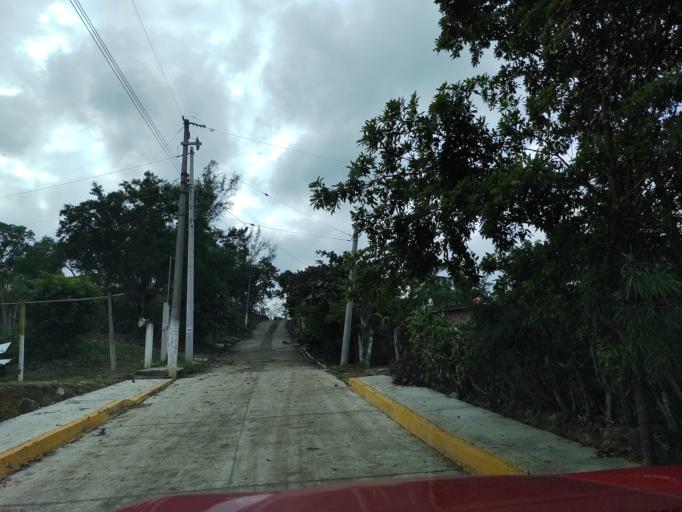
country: MX
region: Veracruz
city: Coatzintla
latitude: 20.4571
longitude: -97.4201
